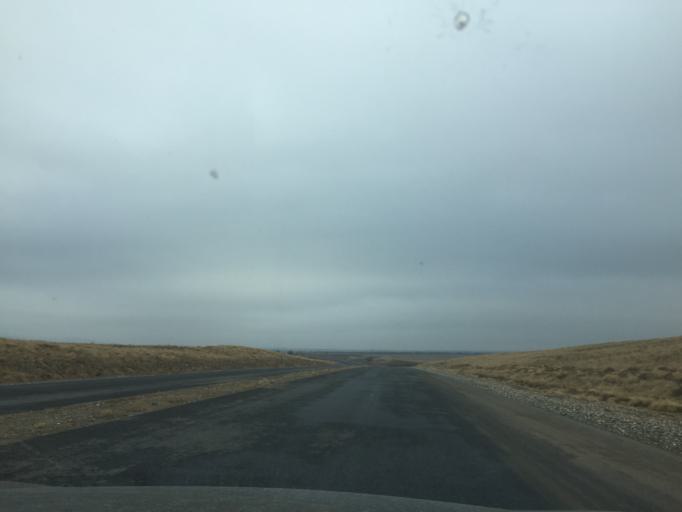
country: KZ
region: Ongtustik Qazaqstan
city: Kokterek
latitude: 42.5440
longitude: 70.1862
